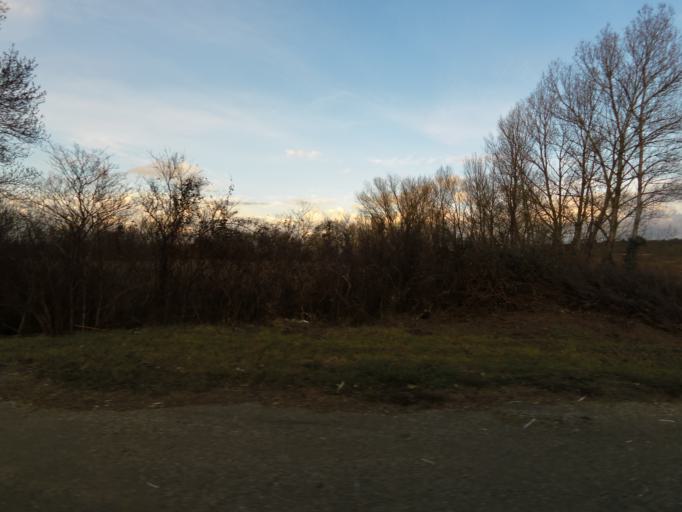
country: FR
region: Languedoc-Roussillon
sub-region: Departement du Gard
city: Saint-Mamert-du-Gard
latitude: 43.9015
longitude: 4.2183
